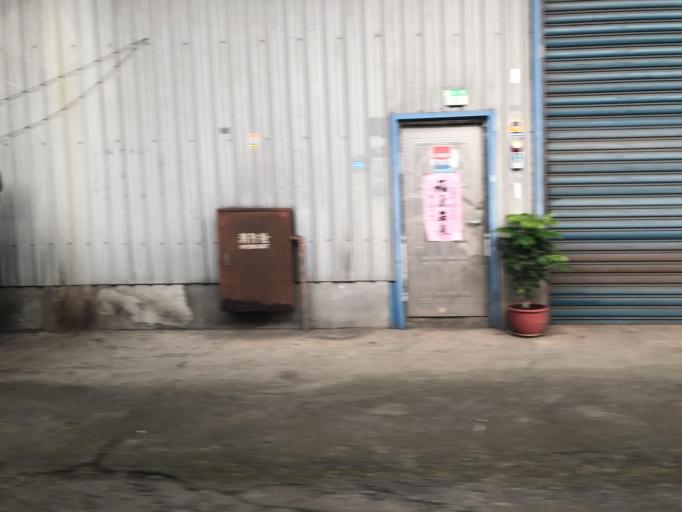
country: TW
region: Taiwan
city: Daxi
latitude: 24.9186
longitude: 121.3631
